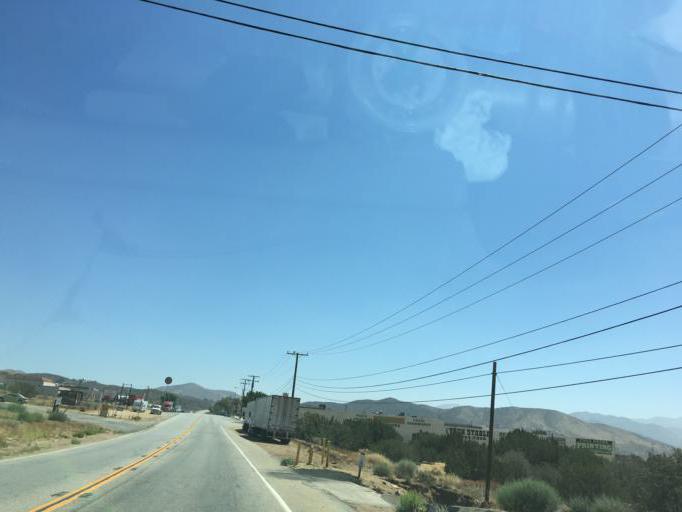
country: US
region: California
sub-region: Los Angeles County
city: Acton
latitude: 34.4925
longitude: -118.2028
